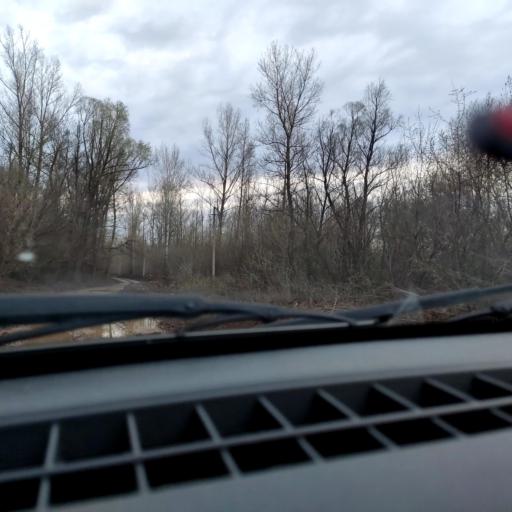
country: RU
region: Bashkortostan
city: Ufa
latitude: 54.6811
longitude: 55.9521
